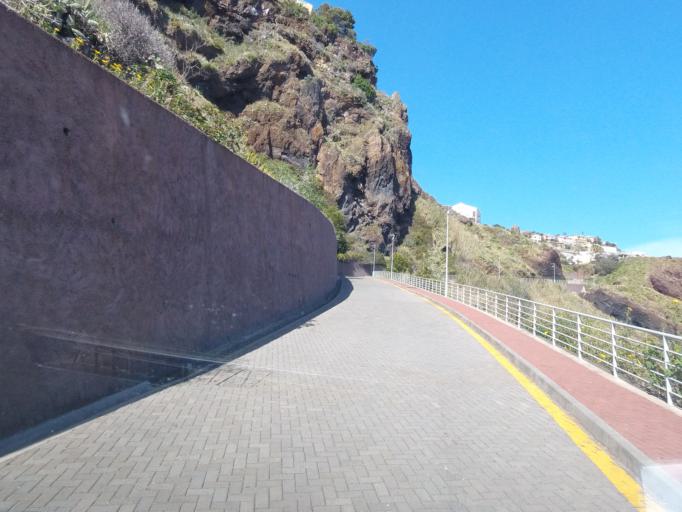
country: PT
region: Madeira
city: Canico
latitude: 32.6401
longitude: -16.8547
